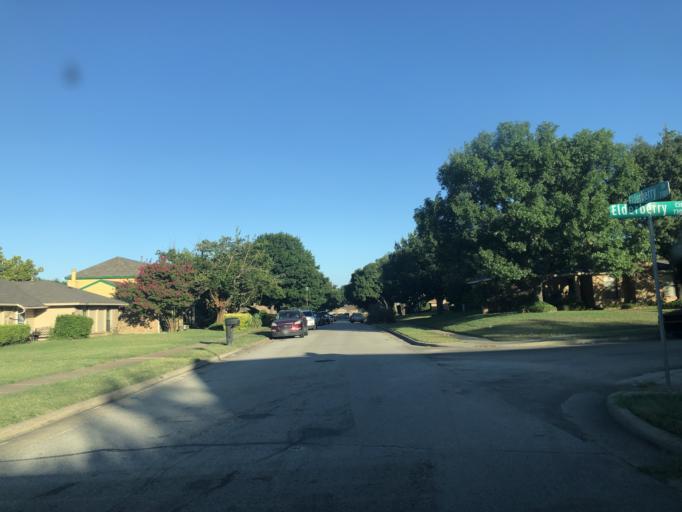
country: US
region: Texas
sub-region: Dallas County
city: Duncanville
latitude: 32.6455
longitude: -96.9481
